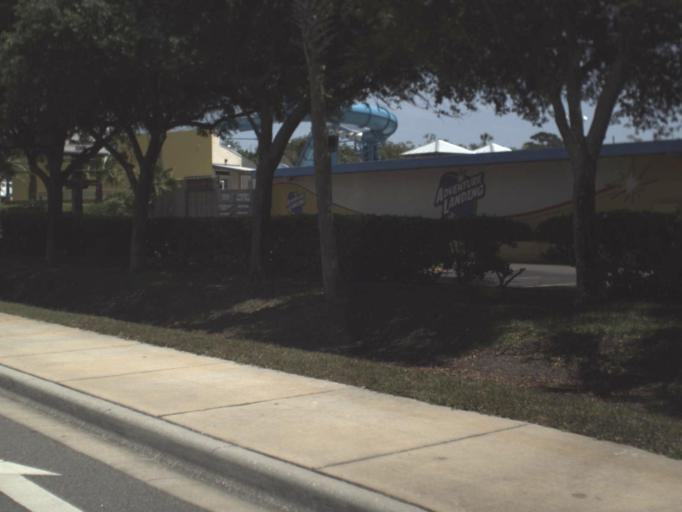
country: US
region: Florida
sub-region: Duval County
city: Jacksonville Beach
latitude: 30.2880
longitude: -81.4134
